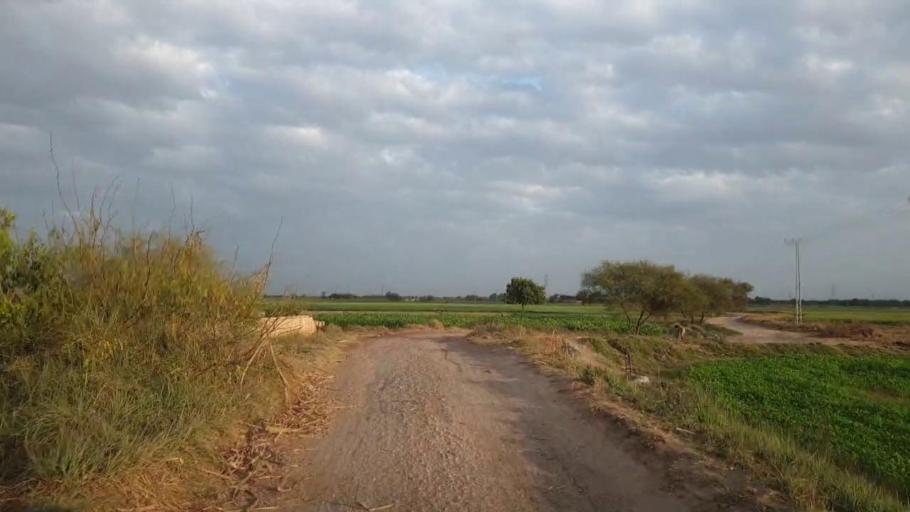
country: PK
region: Sindh
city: Matiari
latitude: 25.5696
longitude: 68.4412
